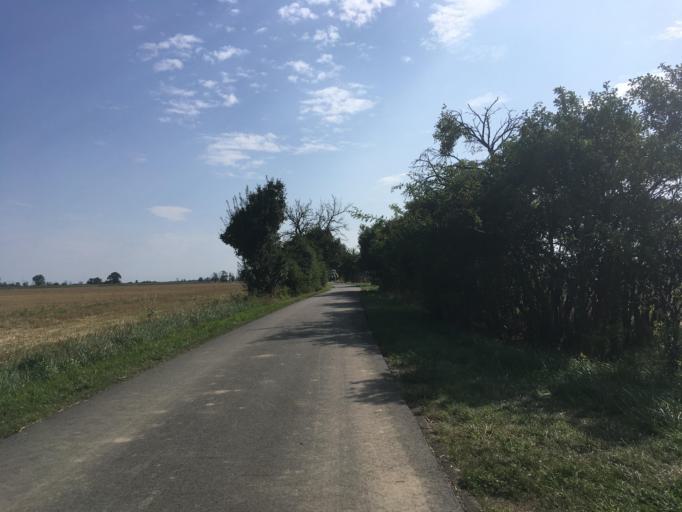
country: DE
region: Saxony
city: Elsnig
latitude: 51.6135
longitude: 12.9323
